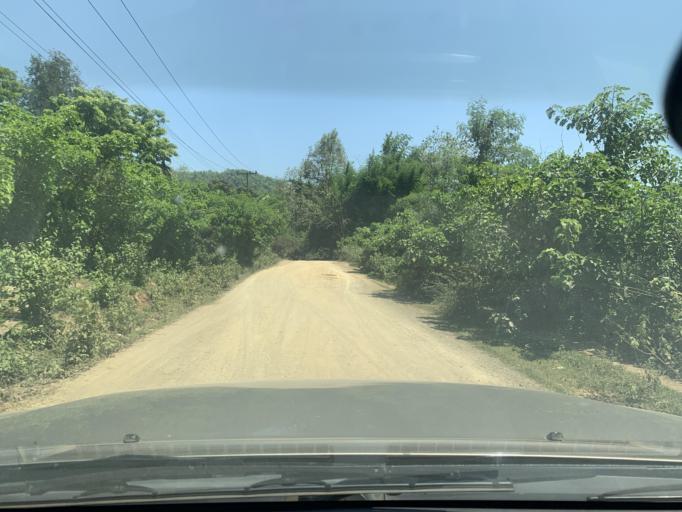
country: LA
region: Louangphabang
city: Louangphabang
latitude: 19.9073
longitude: 102.2332
